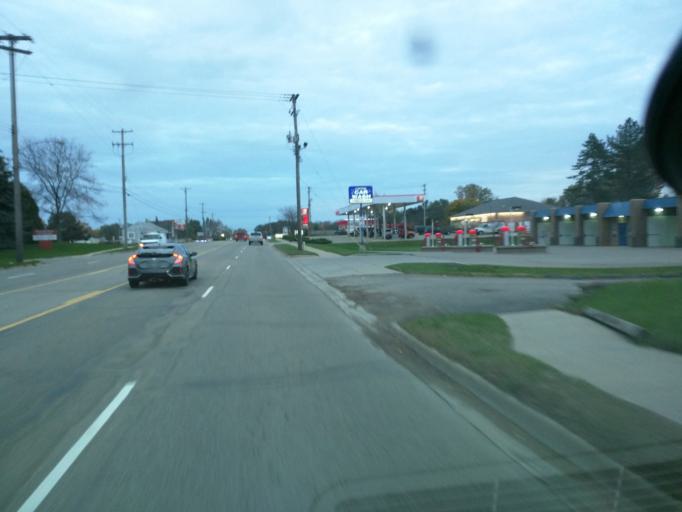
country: US
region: Michigan
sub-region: Ingham County
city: Edgemont Park
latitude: 42.7286
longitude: -84.6029
